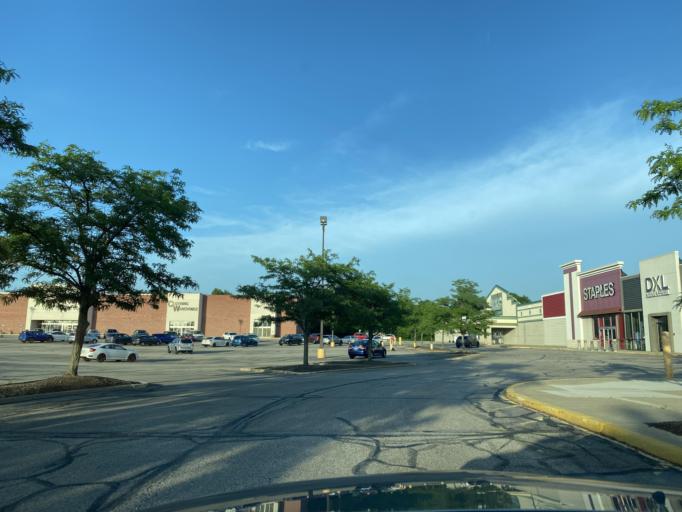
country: US
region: Ohio
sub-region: Summit County
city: Montrose-Ghent
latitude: 41.1317
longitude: -81.6435
